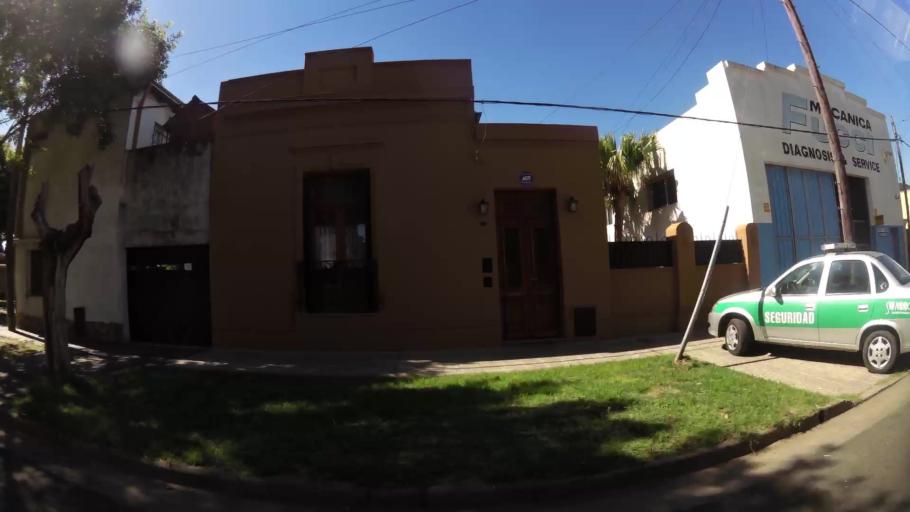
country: AR
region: Santa Fe
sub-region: Departamento de Rosario
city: Rosario
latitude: -32.9355
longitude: -60.7046
